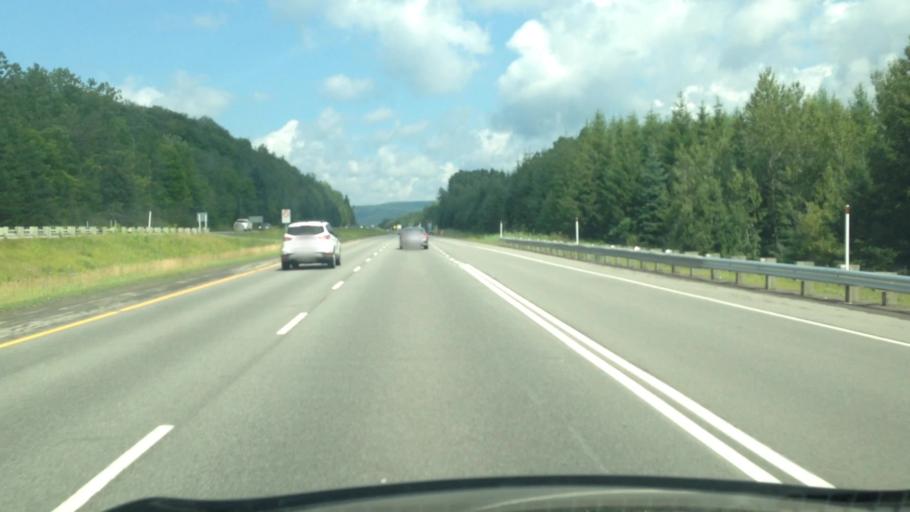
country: CA
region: Quebec
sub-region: Laurentides
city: Prevost
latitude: 45.8451
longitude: -74.0709
